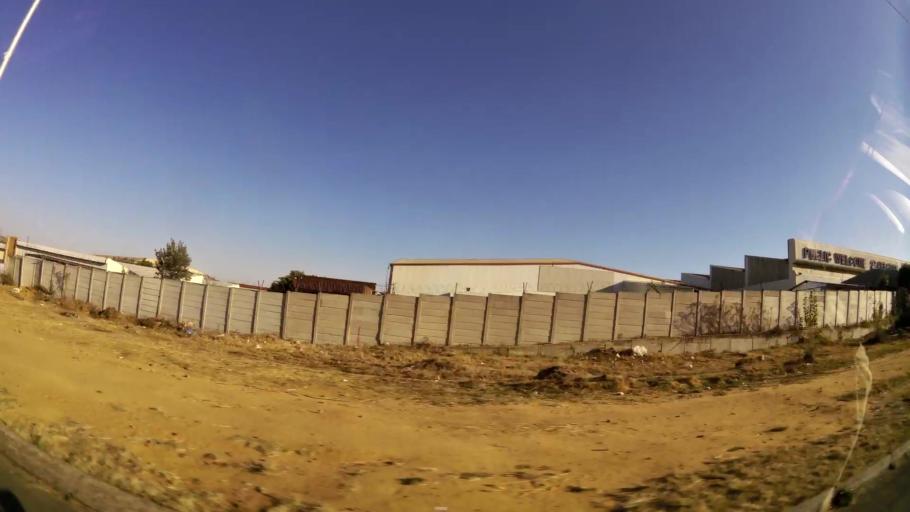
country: ZA
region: Gauteng
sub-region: City of Johannesburg Metropolitan Municipality
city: Roodepoort
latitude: -26.2018
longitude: 27.9462
